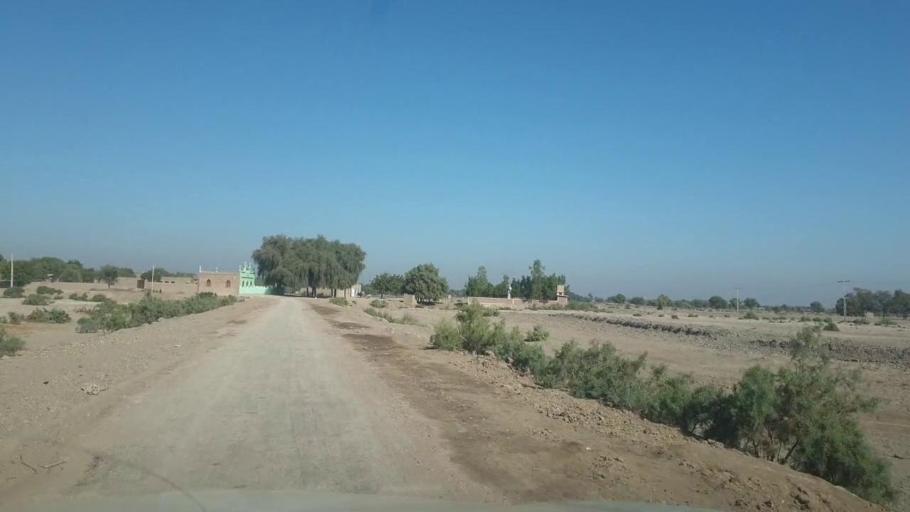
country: PK
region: Sindh
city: Bhan
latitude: 26.5471
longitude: 67.6562
